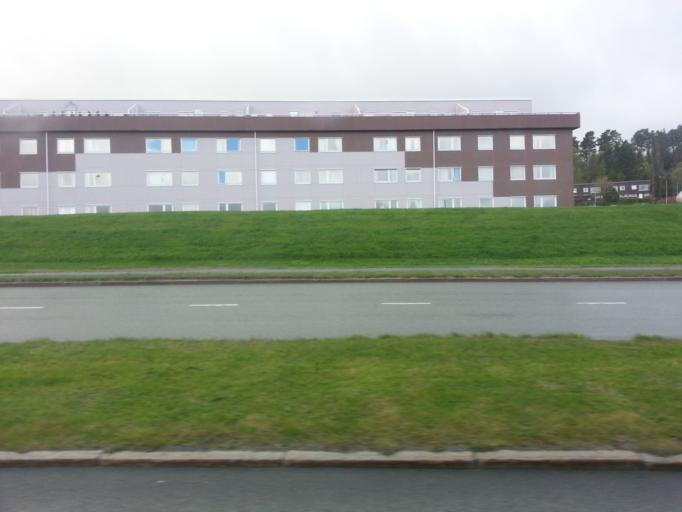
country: NO
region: Sor-Trondelag
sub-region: Trondheim
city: Trondheim
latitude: 63.4109
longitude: 10.3611
